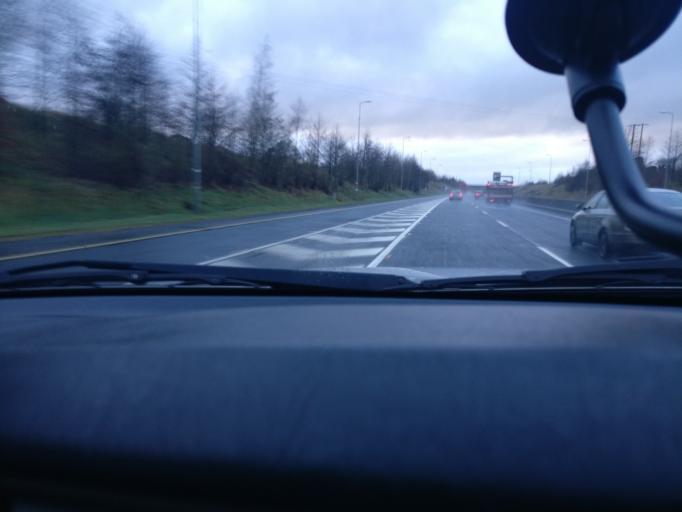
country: IE
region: Leinster
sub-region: An Iarmhi
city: Moate
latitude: 53.3859
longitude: -7.6889
